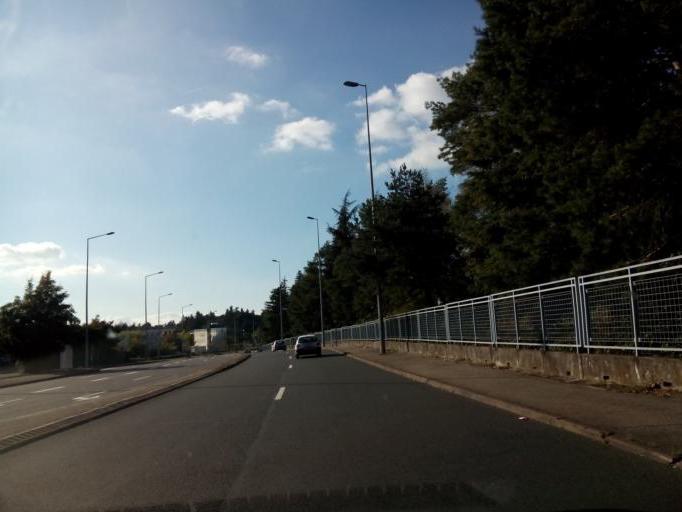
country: FR
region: Rhone-Alpes
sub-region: Departement du Rhone
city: Bron
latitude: 45.7233
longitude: 4.9195
